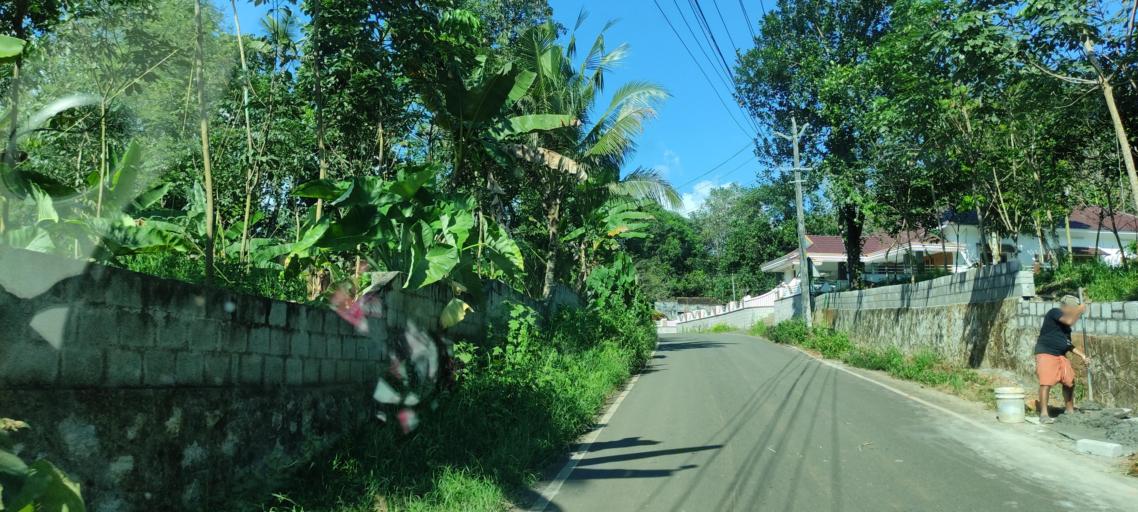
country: IN
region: Kerala
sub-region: Pattanamtitta
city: Adur
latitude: 9.2013
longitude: 76.7485
